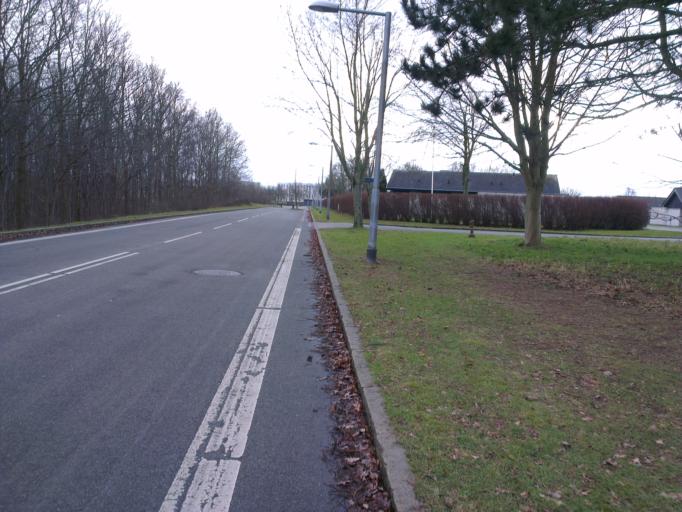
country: DK
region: Capital Region
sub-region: Frederikssund Kommune
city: Frederikssund
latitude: 55.8545
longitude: 12.0510
